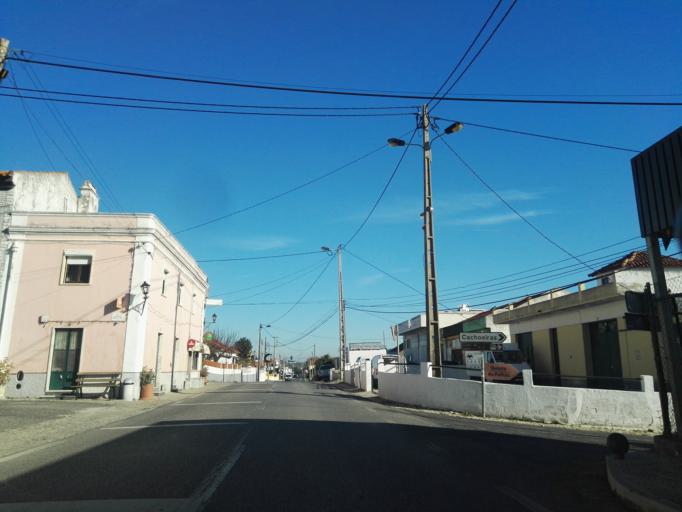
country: PT
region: Lisbon
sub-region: Vila Franca de Xira
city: Castanheira do Ribatejo
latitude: 39.0039
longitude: -9.0043
